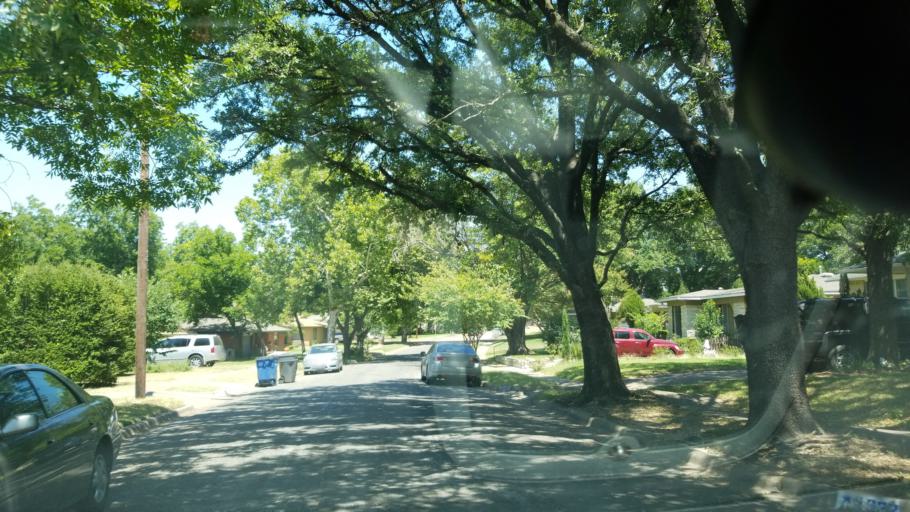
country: US
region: Texas
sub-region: Dallas County
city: Cockrell Hill
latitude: 32.7258
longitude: -96.8522
